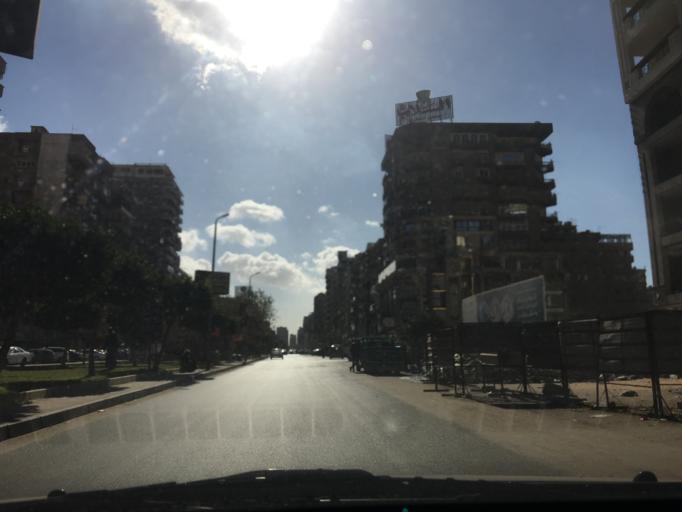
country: EG
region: Muhafazat al Qahirah
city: Cairo
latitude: 30.0588
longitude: 31.3455
